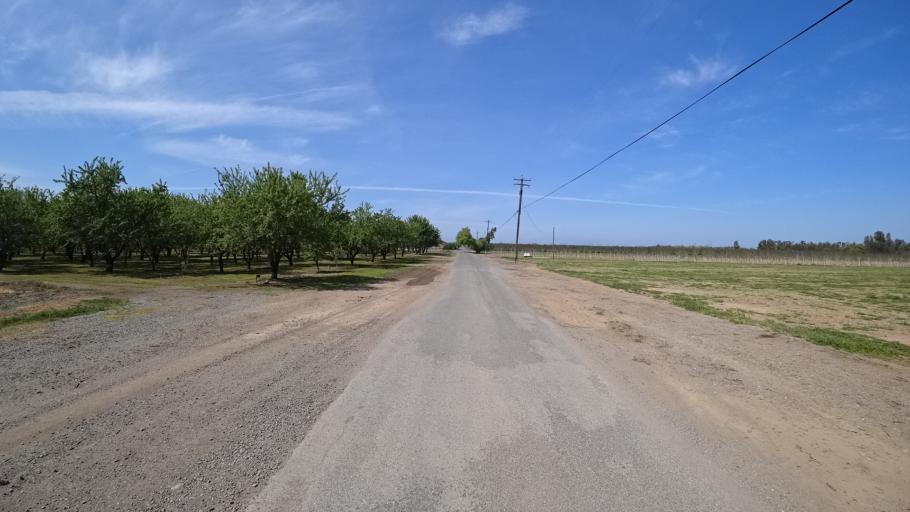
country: US
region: California
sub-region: Glenn County
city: Hamilton City
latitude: 39.8042
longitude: -122.0632
